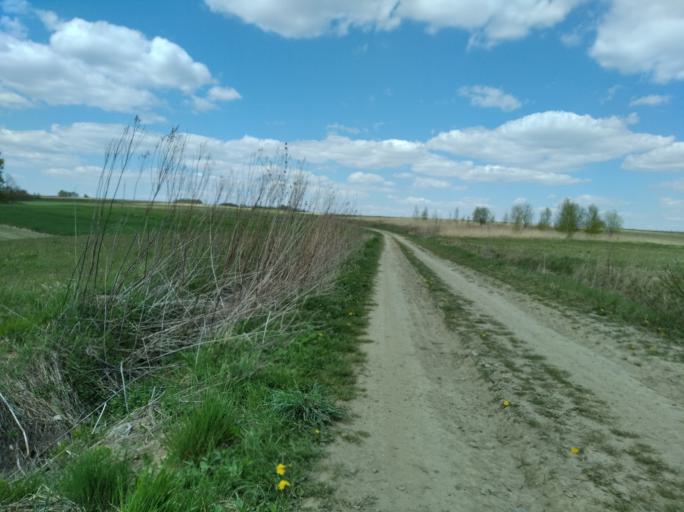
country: PL
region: Subcarpathian Voivodeship
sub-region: Powiat brzozowski
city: Golcowa
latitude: 49.7579
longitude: 22.0698
